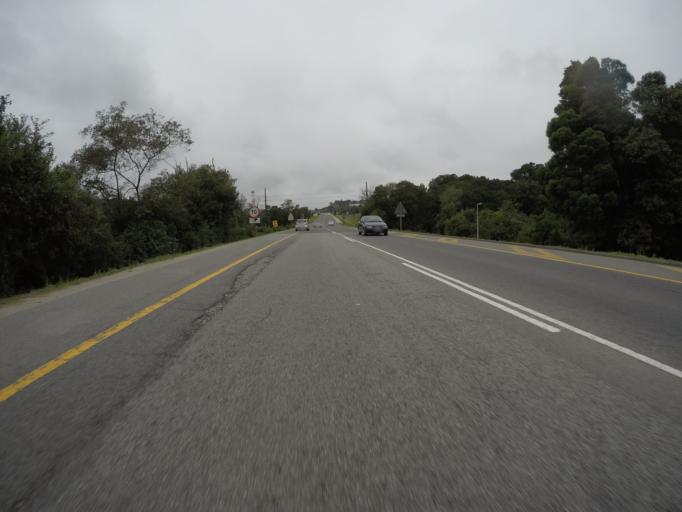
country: ZA
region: Western Cape
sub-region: Eden District Municipality
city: Knysna
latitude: -34.0415
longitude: 23.0777
